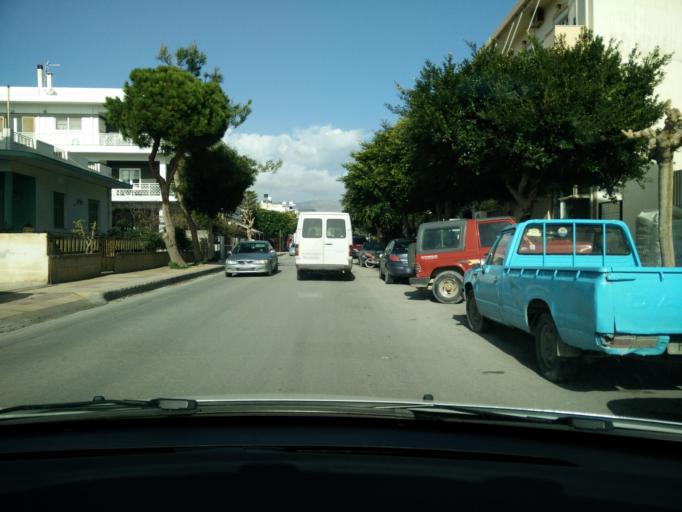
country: GR
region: Crete
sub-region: Nomos Lasithiou
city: Ierapetra
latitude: 35.0093
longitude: 25.7356
